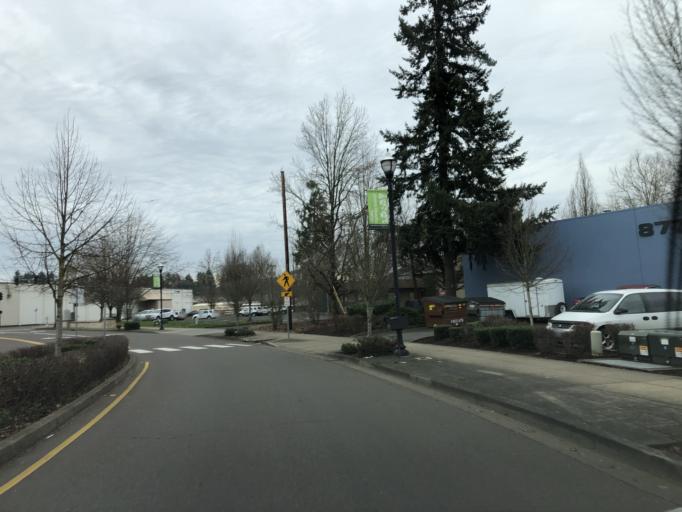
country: US
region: Oregon
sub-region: Washington County
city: Tigard
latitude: 45.4265
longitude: -122.7674
